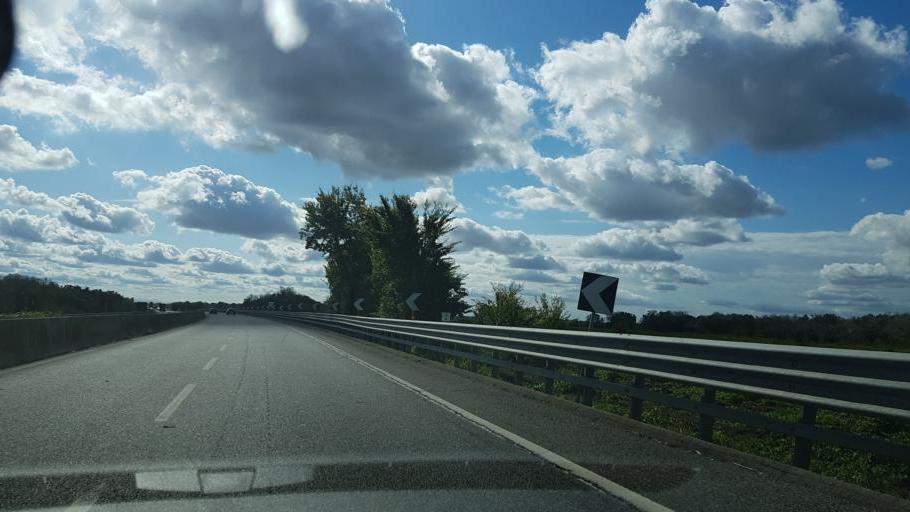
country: IT
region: Apulia
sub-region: Provincia di Brindisi
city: San Pietro Vernotico
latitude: 40.5425
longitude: 18.0014
